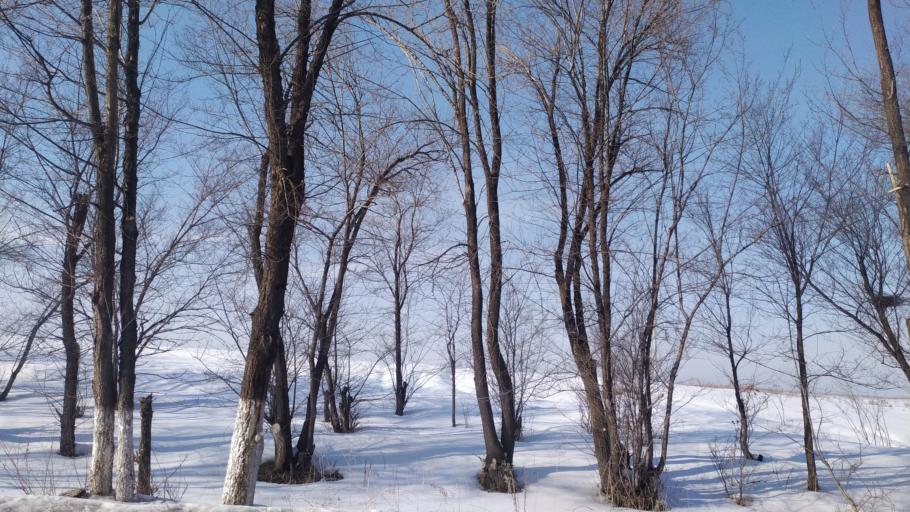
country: KZ
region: Almaty Oblysy
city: Burunday
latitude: 43.2583
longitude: 76.4686
